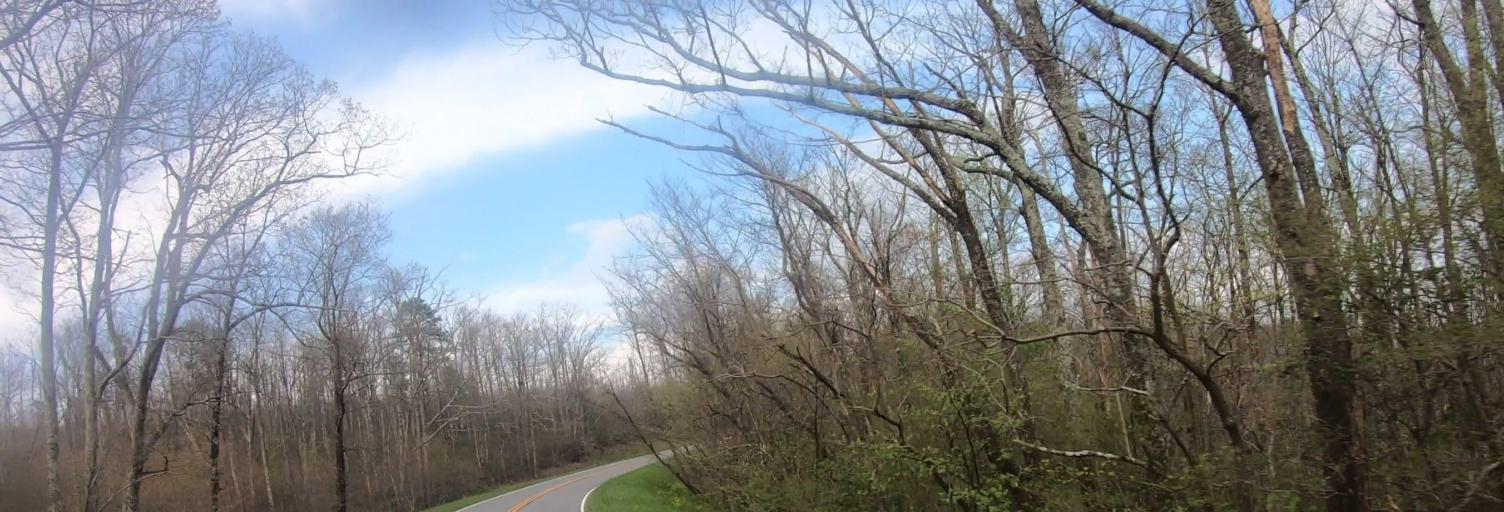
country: US
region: Virginia
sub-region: Rockingham County
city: Grottoes
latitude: 38.2097
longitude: -78.7353
